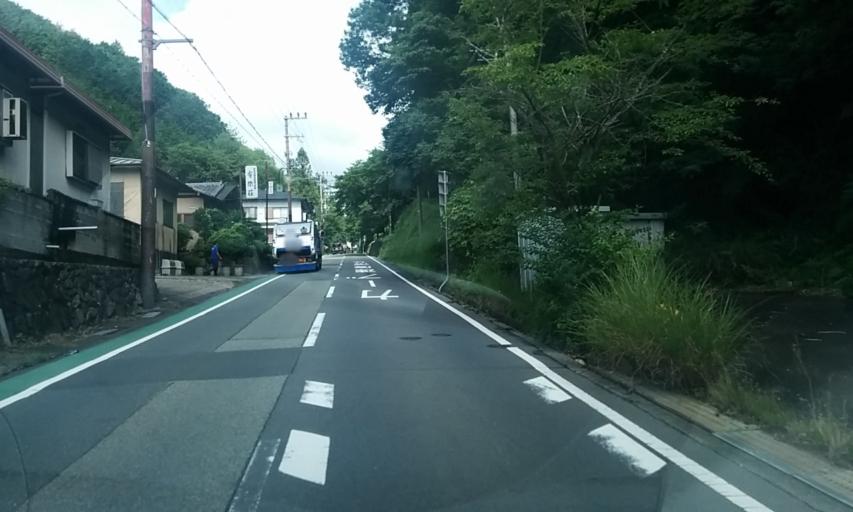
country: JP
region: Kyoto
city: Kameoka
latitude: 35.0186
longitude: 135.5187
